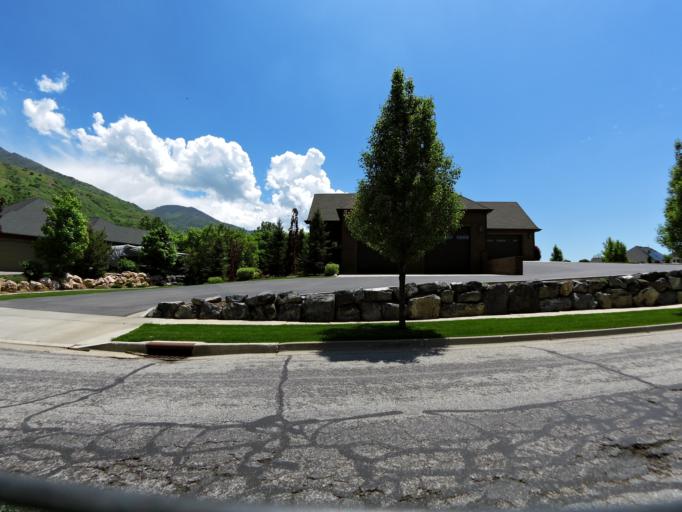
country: US
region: Utah
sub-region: Weber County
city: Uintah
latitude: 41.1632
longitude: -111.9241
